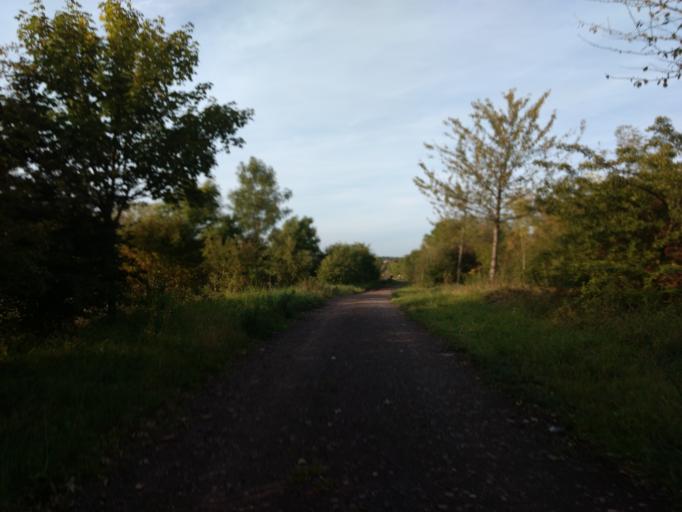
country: DE
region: Saarland
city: Ensdorf
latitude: 49.3108
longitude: 6.7709
